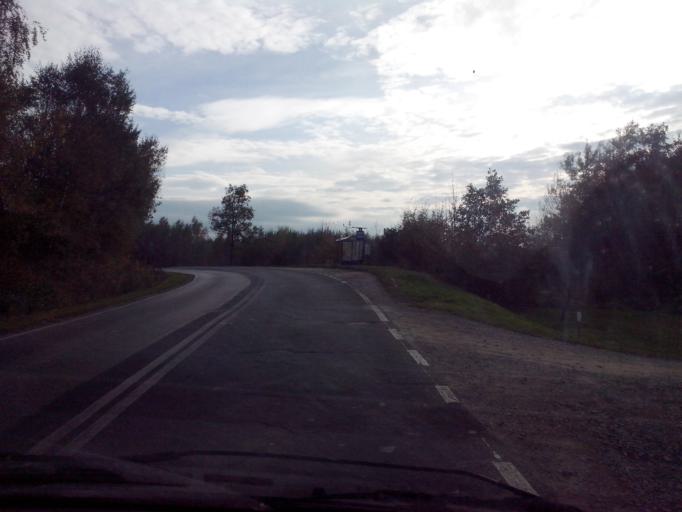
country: PL
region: Subcarpathian Voivodeship
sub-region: Powiat ropczycko-sedziszowski
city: Wielopole Skrzynskie
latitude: 49.9160
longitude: 21.6144
